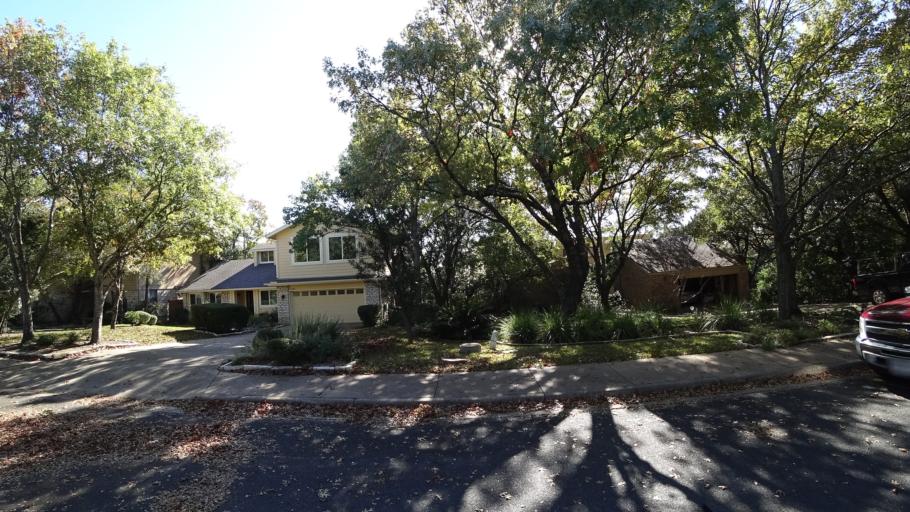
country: US
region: Texas
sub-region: Williamson County
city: Jollyville
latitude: 30.4194
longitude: -97.7738
